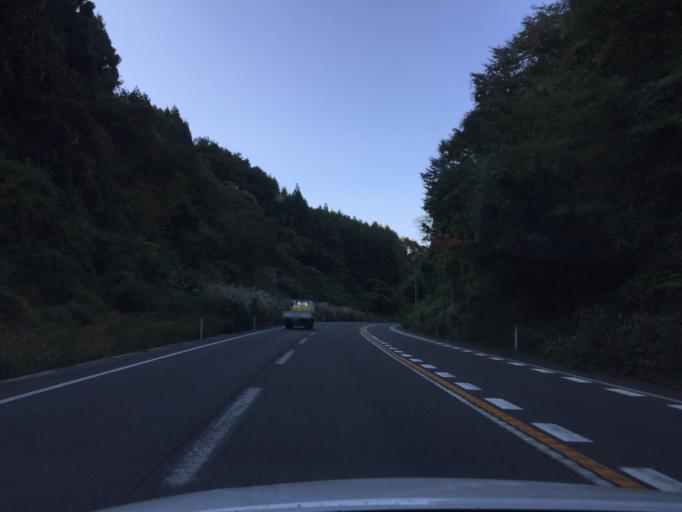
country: JP
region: Fukushima
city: Ishikawa
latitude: 37.1664
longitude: 140.6574
